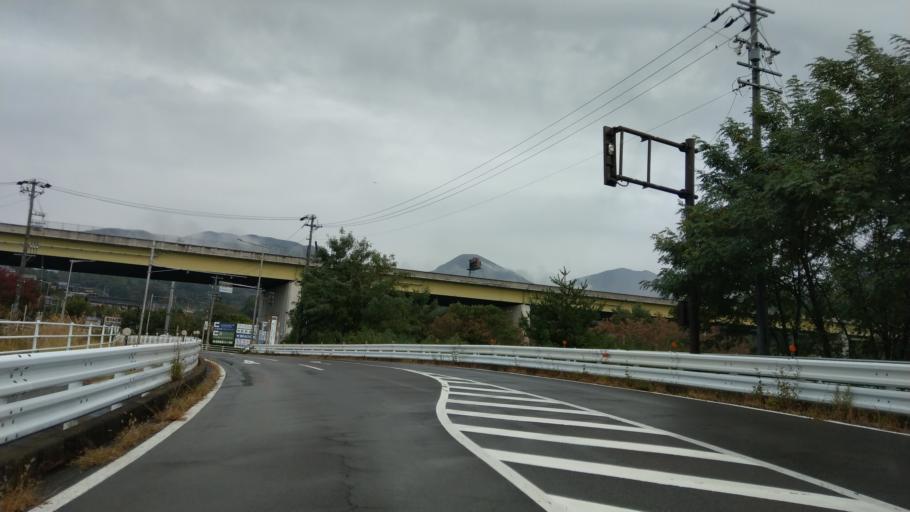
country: JP
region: Nagano
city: Komoro
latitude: 36.3442
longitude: 138.4110
